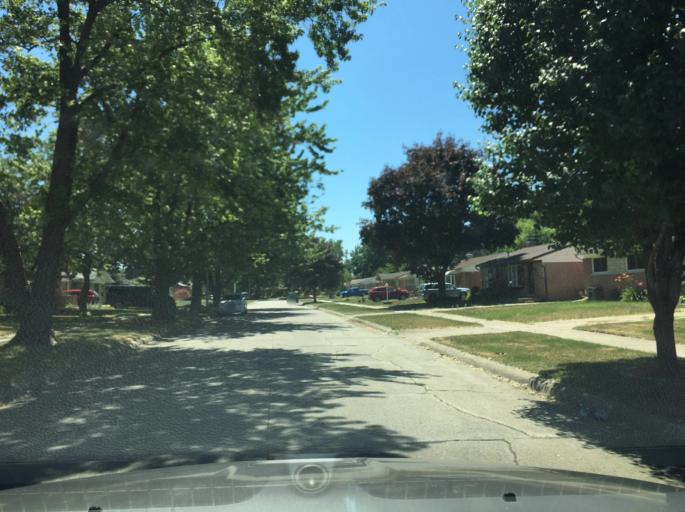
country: US
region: Michigan
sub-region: Macomb County
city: Fraser
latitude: 42.5425
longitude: -82.9242
